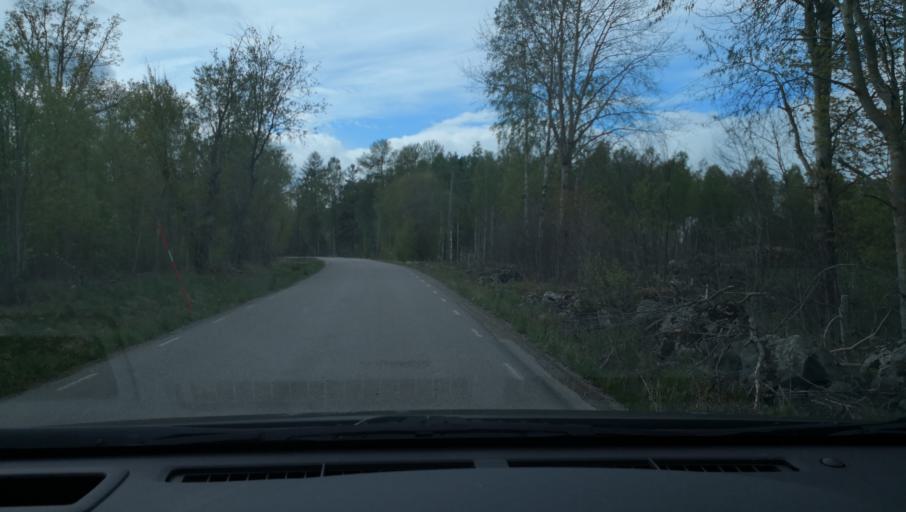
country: SE
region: OErebro
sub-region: Kumla Kommun
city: Hallabrottet
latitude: 59.1576
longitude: 15.2120
